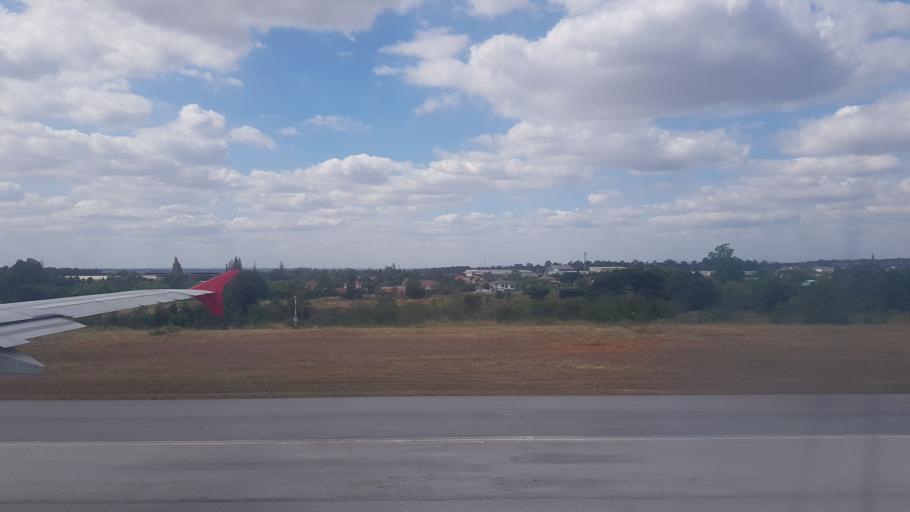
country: TH
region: Khon Kaen
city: Khon Kaen
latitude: 16.4569
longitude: 102.7773
